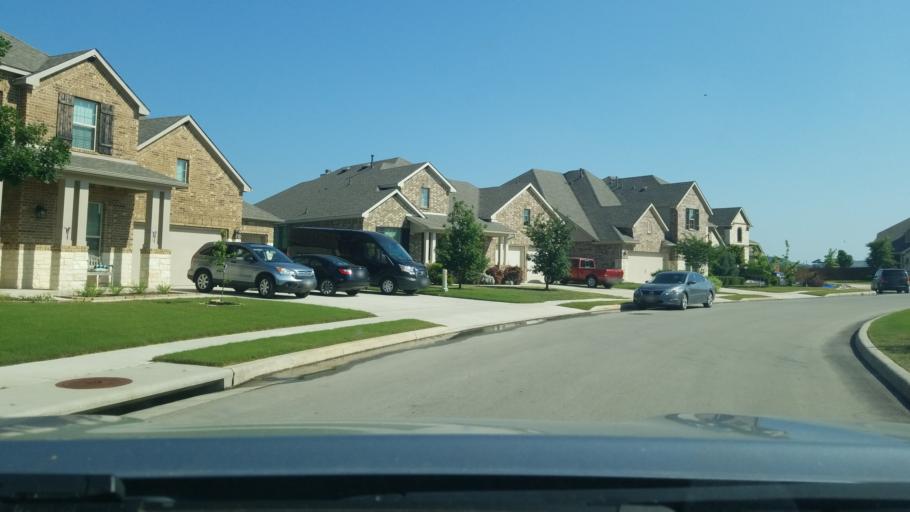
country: US
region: Texas
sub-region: Comal County
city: Bulverde
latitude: 29.7505
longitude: -98.4179
